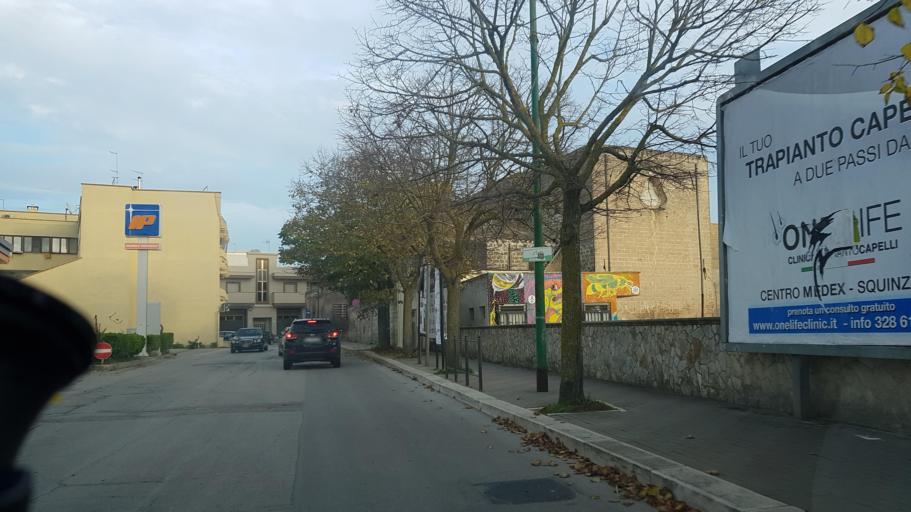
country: IT
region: Apulia
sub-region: Provincia di Brindisi
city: Latiano
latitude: 40.5565
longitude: 17.7167
